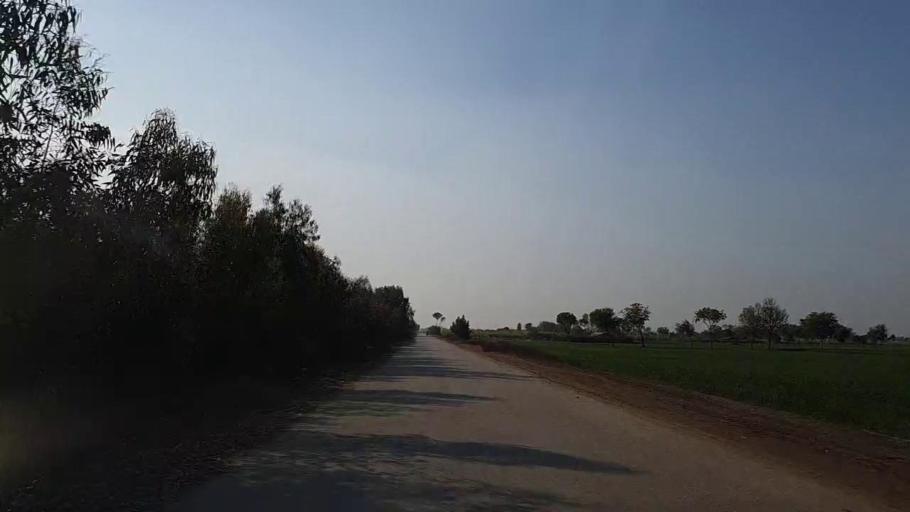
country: PK
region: Sindh
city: Daur
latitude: 26.4040
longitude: 68.2809
